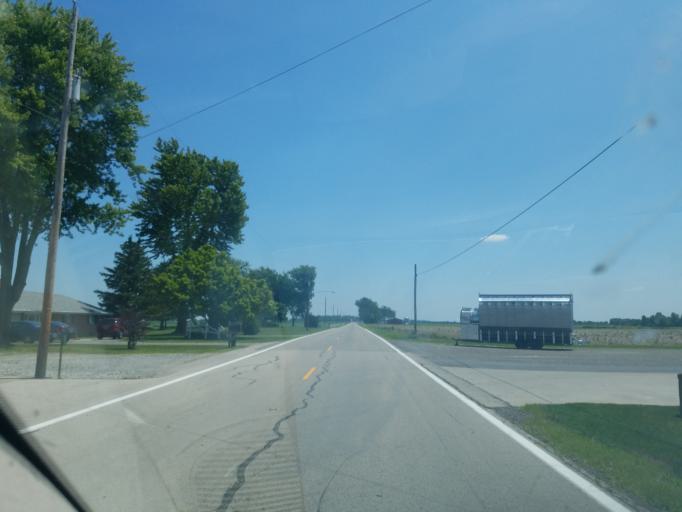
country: US
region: Ohio
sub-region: Allen County
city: Spencerville
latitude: 40.7426
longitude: -84.4751
